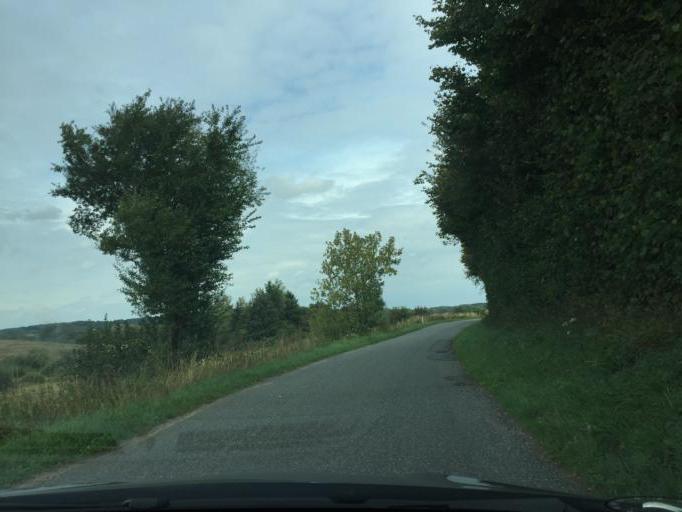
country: DK
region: South Denmark
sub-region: Assens Kommune
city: Vissenbjerg
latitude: 55.3533
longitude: 10.1098
